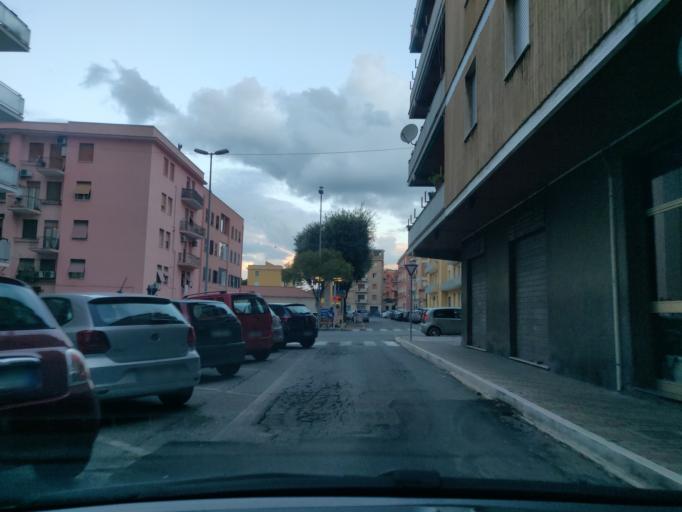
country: IT
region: Latium
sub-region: Citta metropolitana di Roma Capitale
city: Civitavecchia
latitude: 42.0945
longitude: 11.8003
